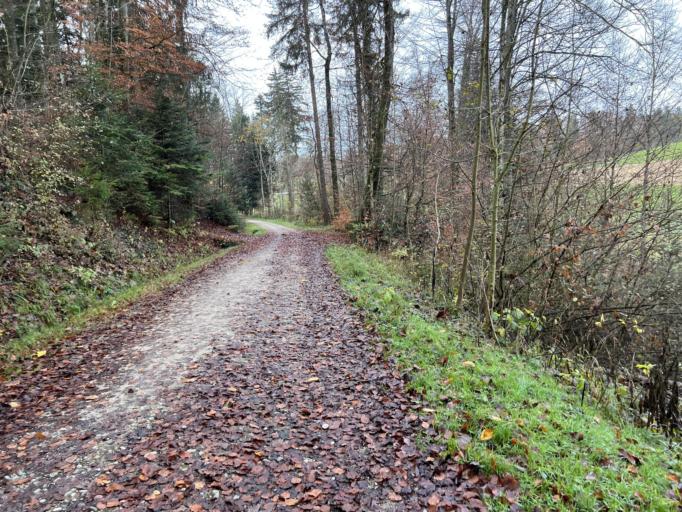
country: CH
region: Zurich
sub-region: Bezirk Meilen
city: Oetwil am See
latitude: 47.2577
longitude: 8.7302
